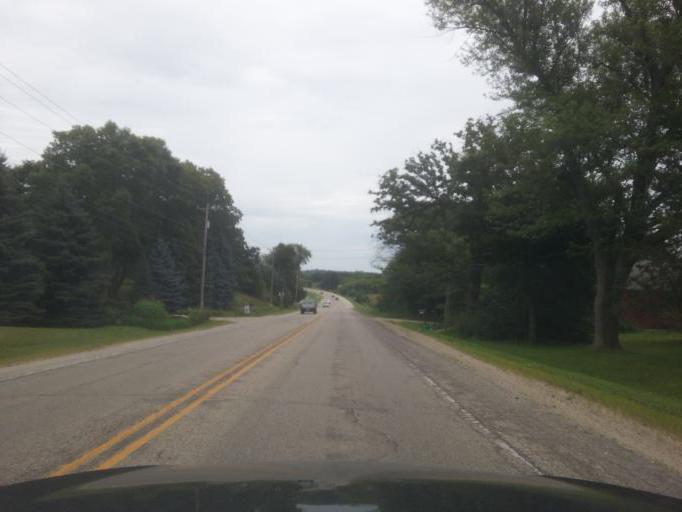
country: US
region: Wisconsin
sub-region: Dane County
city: Cottage Grove
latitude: 43.0850
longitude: -89.2640
